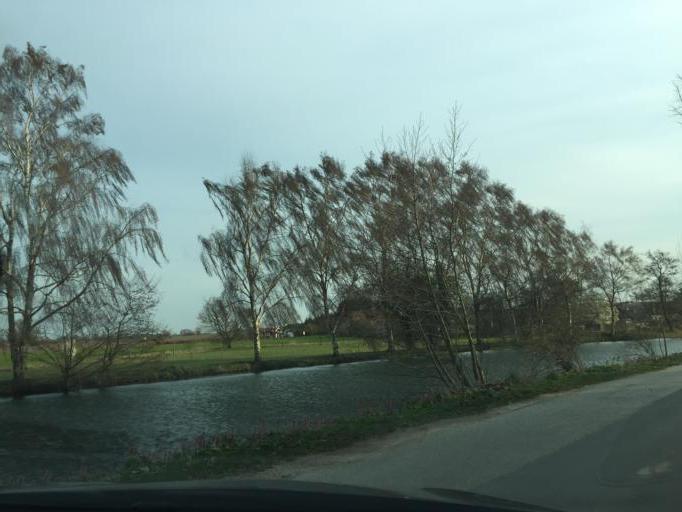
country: DK
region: South Denmark
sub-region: Kerteminde Kommune
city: Langeskov
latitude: 55.3424
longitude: 10.5478
